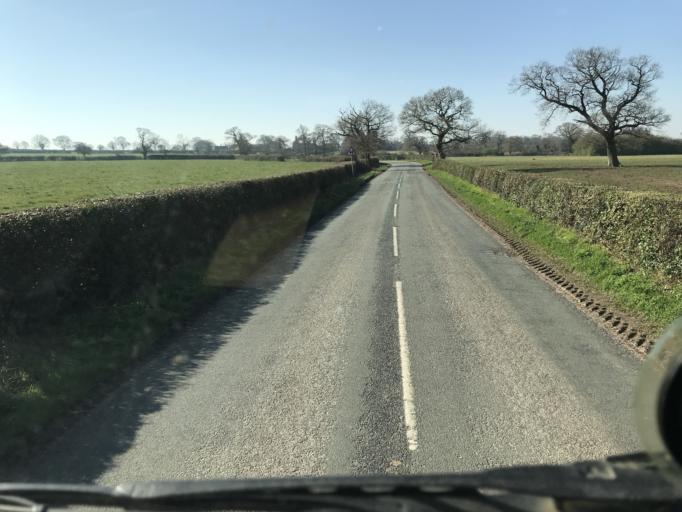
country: GB
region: England
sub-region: Cheshire West and Chester
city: Waverton
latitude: 53.1595
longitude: -2.8288
